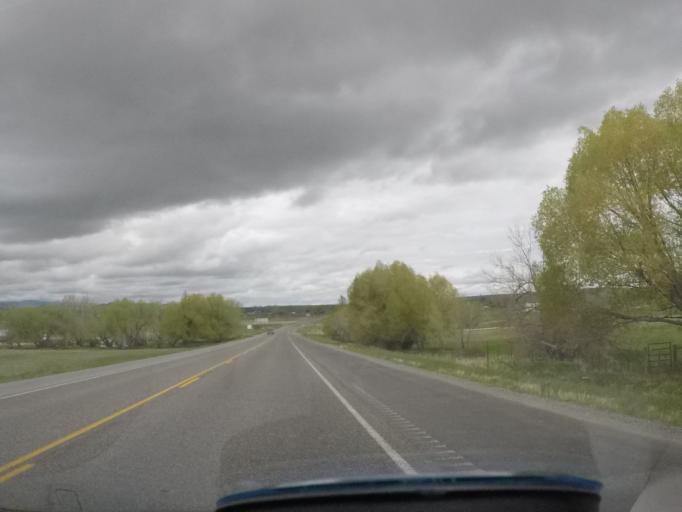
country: US
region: Wyoming
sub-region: Fremont County
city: Lander
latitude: 42.8644
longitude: -108.7761
